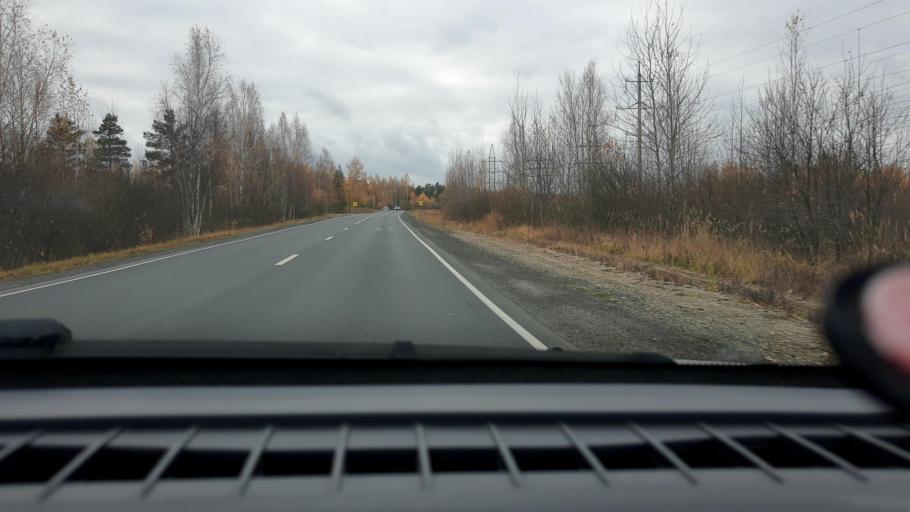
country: RU
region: Nizjnij Novgorod
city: Lukino
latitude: 56.3693
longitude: 43.6181
